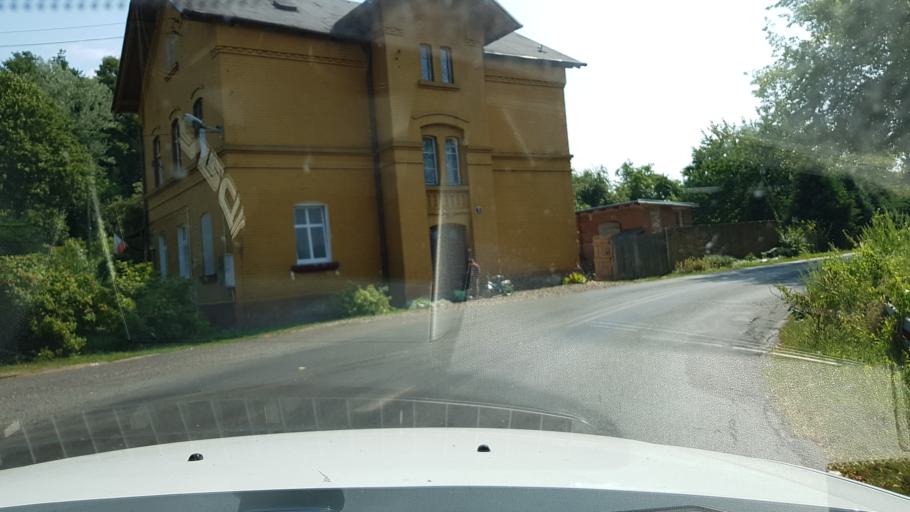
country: PL
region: West Pomeranian Voivodeship
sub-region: Powiat gryfinski
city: Cedynia
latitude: 52.8210
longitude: 14.2349
